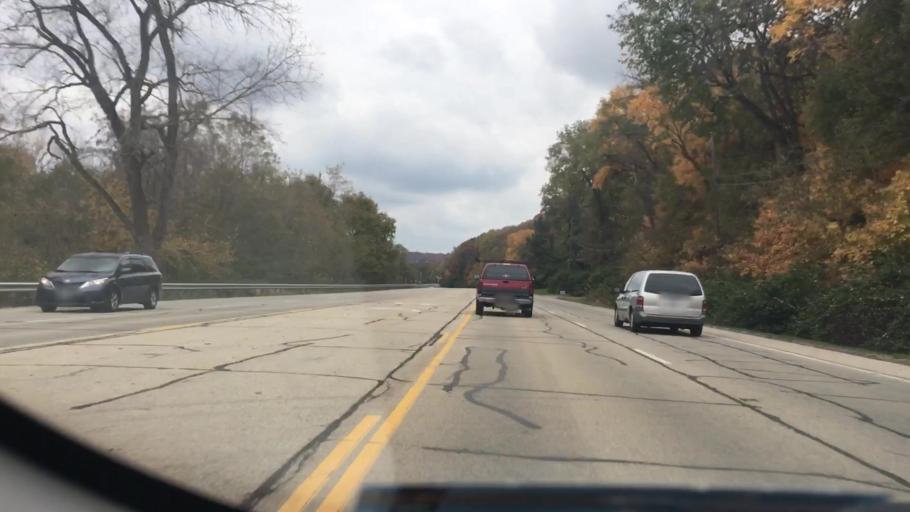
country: US
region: Illinois
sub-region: Peoria County
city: Peoria Heights
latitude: 40.7826
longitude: -89.5774
